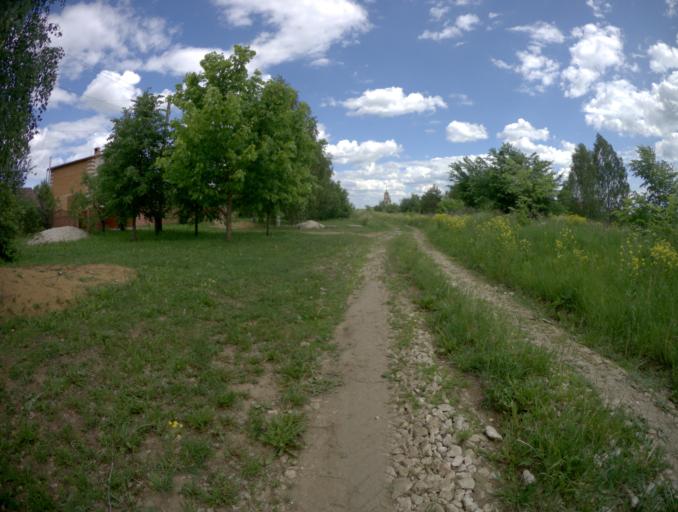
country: RU
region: Vladimir
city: Suzdal'
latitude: 56.4407
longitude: 40.3802
